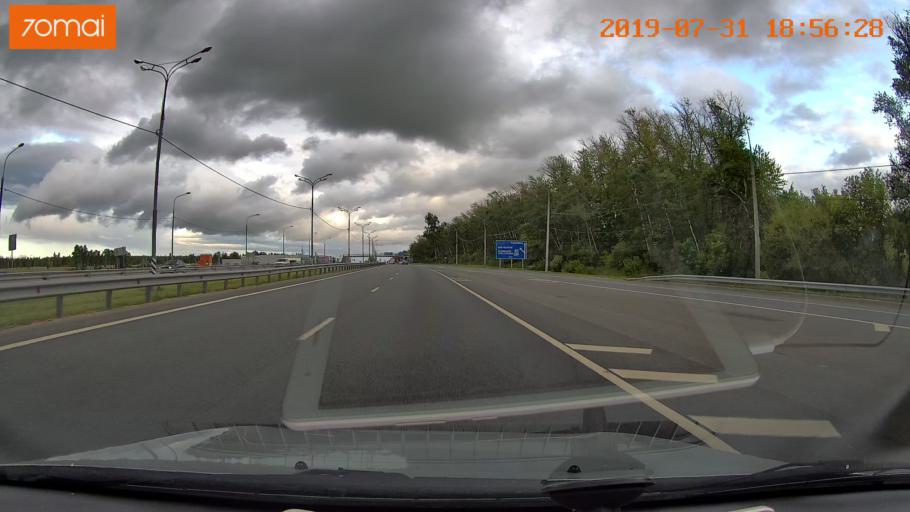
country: RU
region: Moskovskaya
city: Raduzhnyy
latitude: 55.1628
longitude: 38.6784
